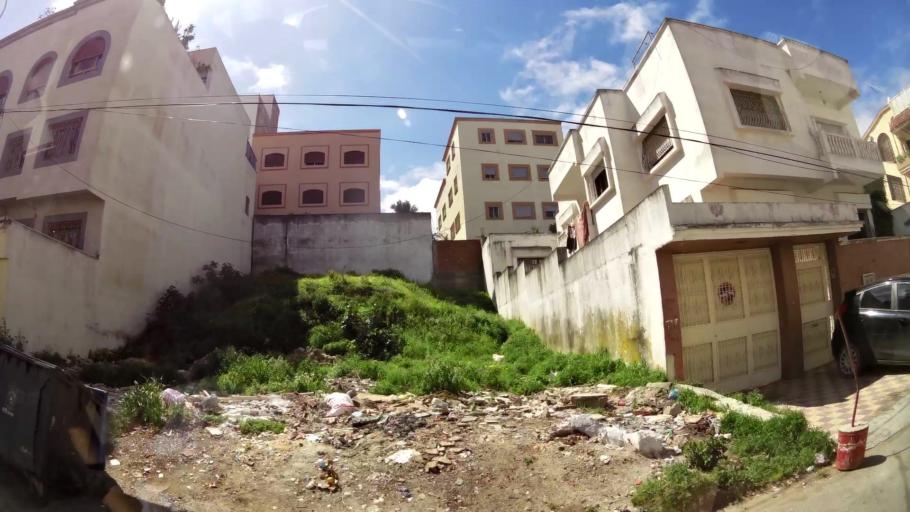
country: MA
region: Tanger-Tetouan
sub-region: Tanger-Assilah
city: Tangier
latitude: 35.7840
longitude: -5.8268
